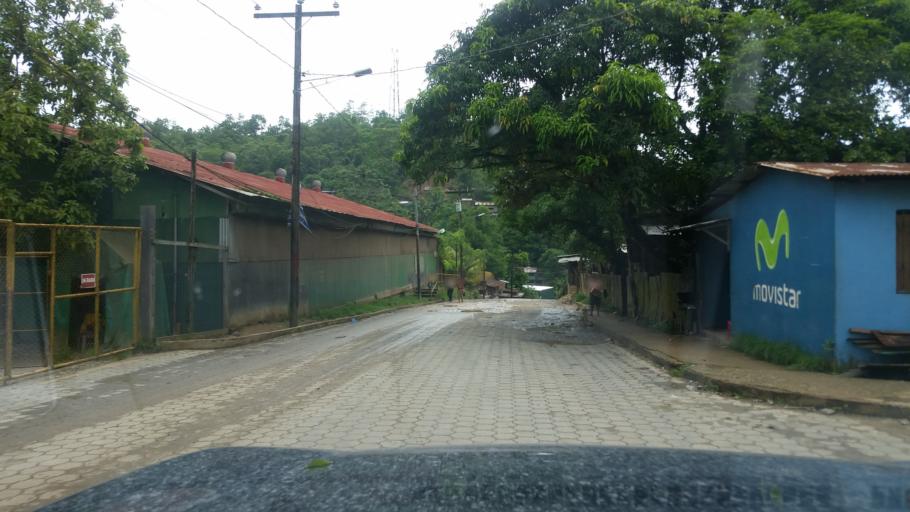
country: NI
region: Atlantico Norte (RAAN)
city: Bonanza
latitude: 14.0297
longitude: -84.5961
